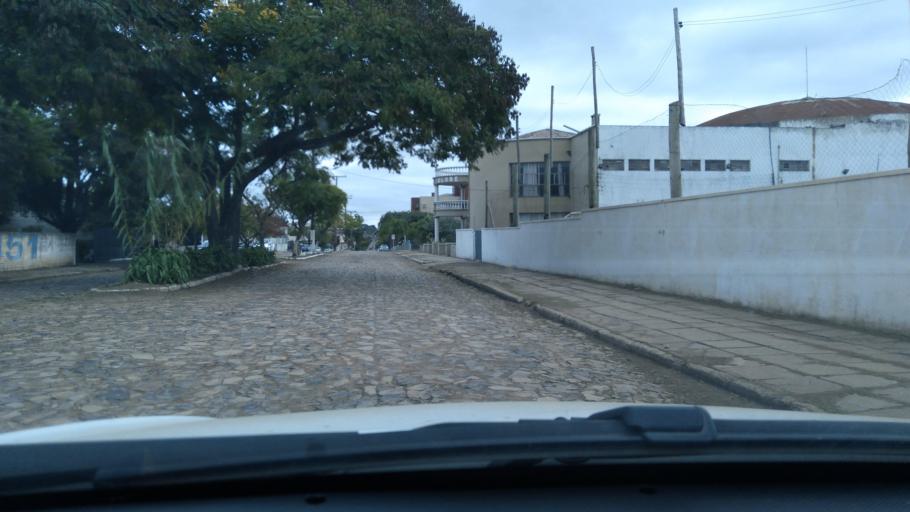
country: BR
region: Rio Grande do Sul
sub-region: Dom Pedrito
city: Dom Pedrito
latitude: -30.9866
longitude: -54.6638
